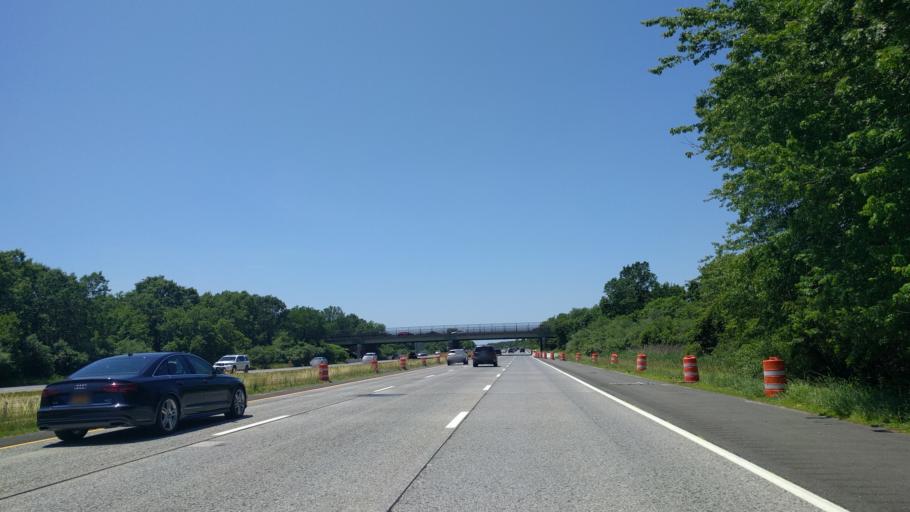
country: US
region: New York
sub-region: Suffolk County
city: Manorville
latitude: 40.8643
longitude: -72.8203
